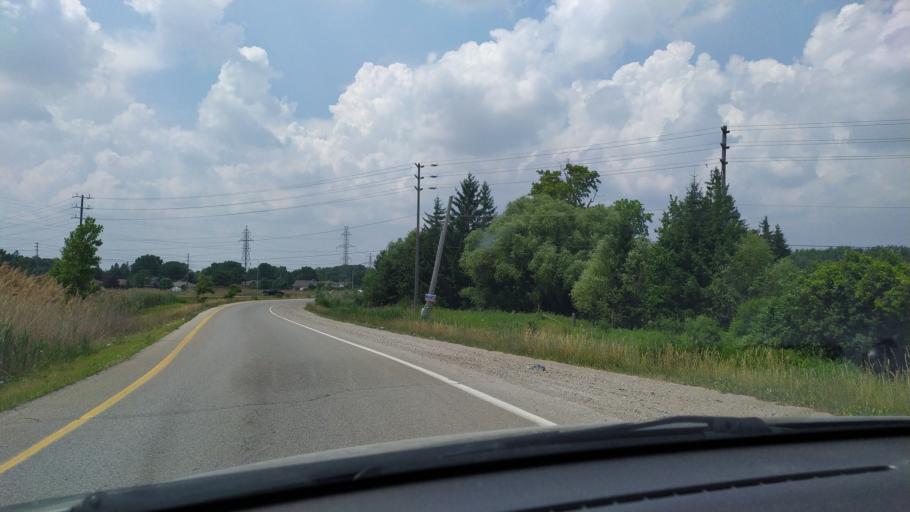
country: CA
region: Ontario
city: London
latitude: 42.9466
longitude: -81.1835
